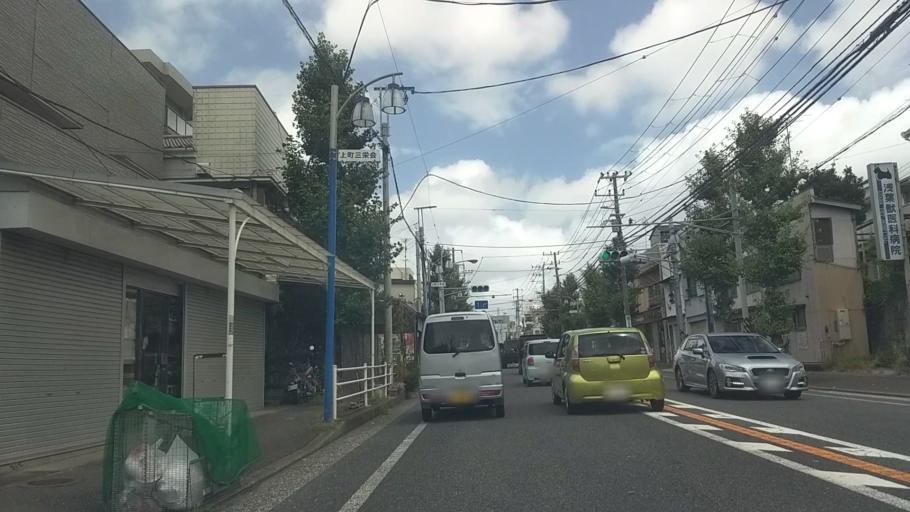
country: JP
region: Kanagawa
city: Yokosuka
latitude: 35.2700
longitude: 139.6715
